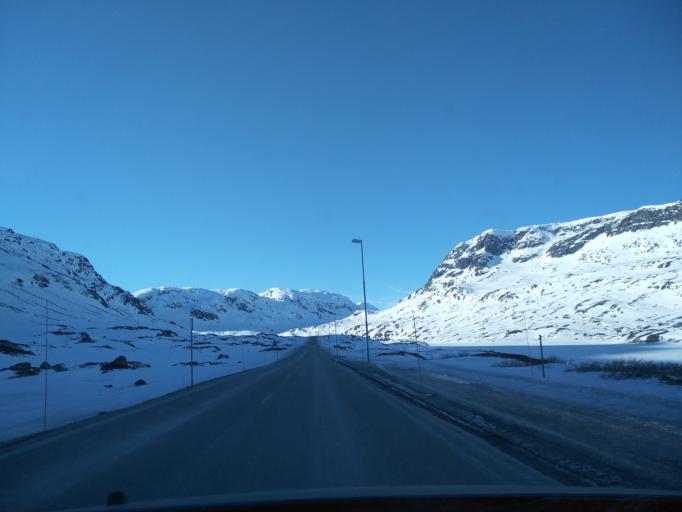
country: NO
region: Aust-Agder
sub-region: Bykle
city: Hovden
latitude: 59.8489
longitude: 7.1234
